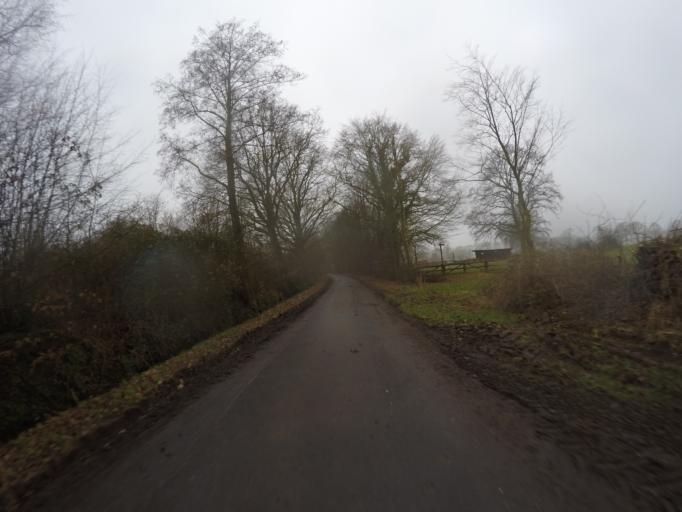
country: DE
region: Schleswig-Holstein
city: Quickborn
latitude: 53.7168
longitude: 9.9000
